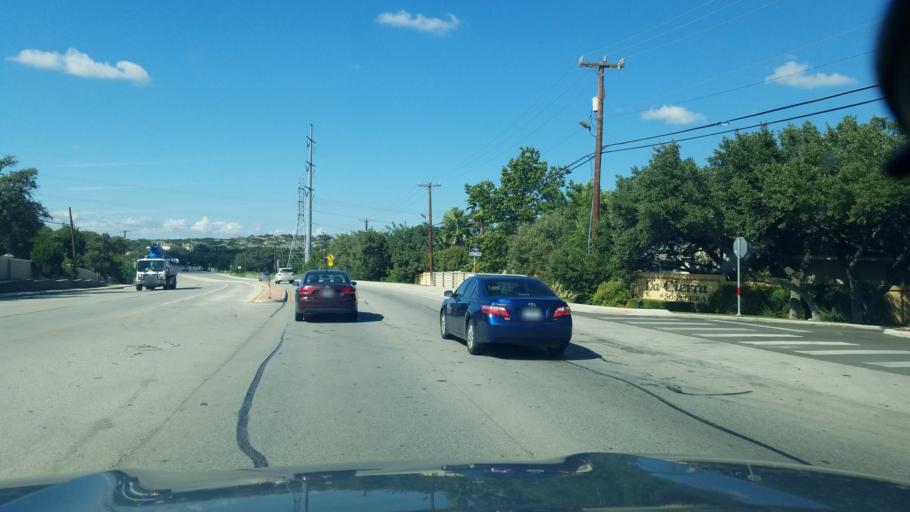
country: US
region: Texas
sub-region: Bexar County
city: Hollywood Park
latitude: 29.6162
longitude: -98.5099
